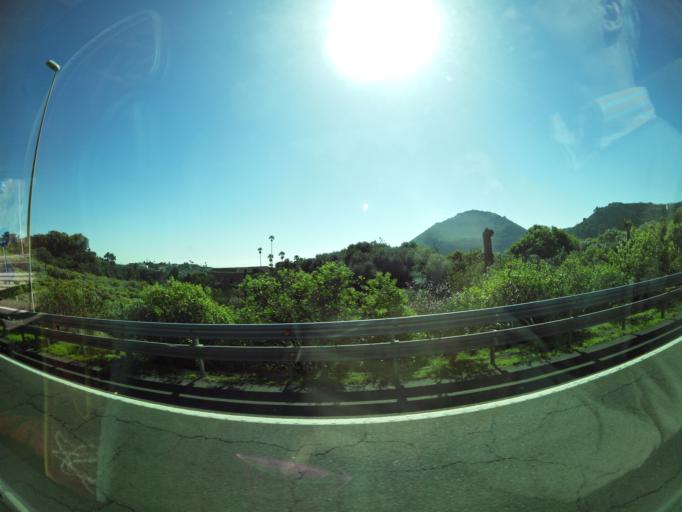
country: ES
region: Canary Islands
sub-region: Provincia de Las Palmas
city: Santa Brigida
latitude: 28.0496
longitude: -15.4650
